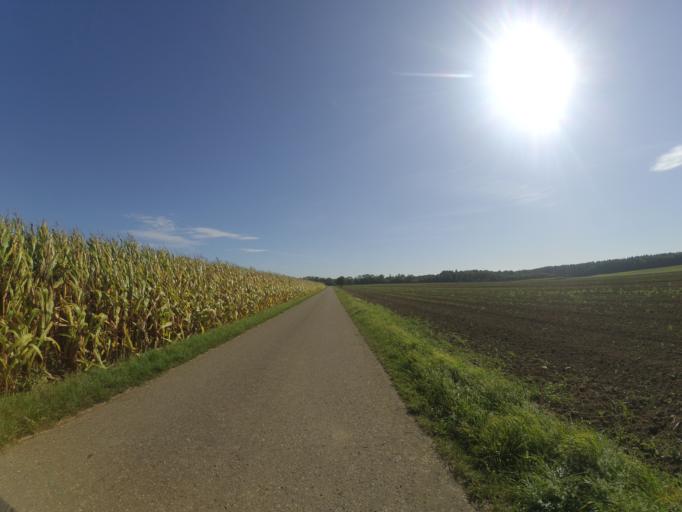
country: DE
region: Baden-Wuerttemberg
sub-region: Tuebingen Region
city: Neenstetten
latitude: 48.5447
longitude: 10.0291
